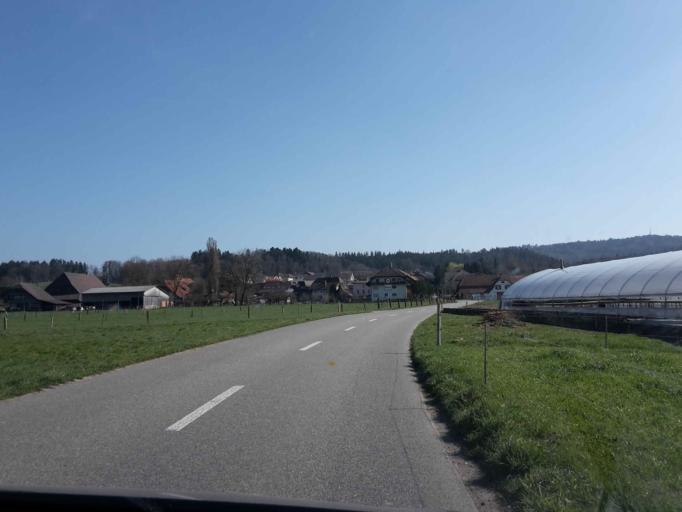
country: CH
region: Bern
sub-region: Oberaargau
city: Lotzwil
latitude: 47.1873
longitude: 7.7518
